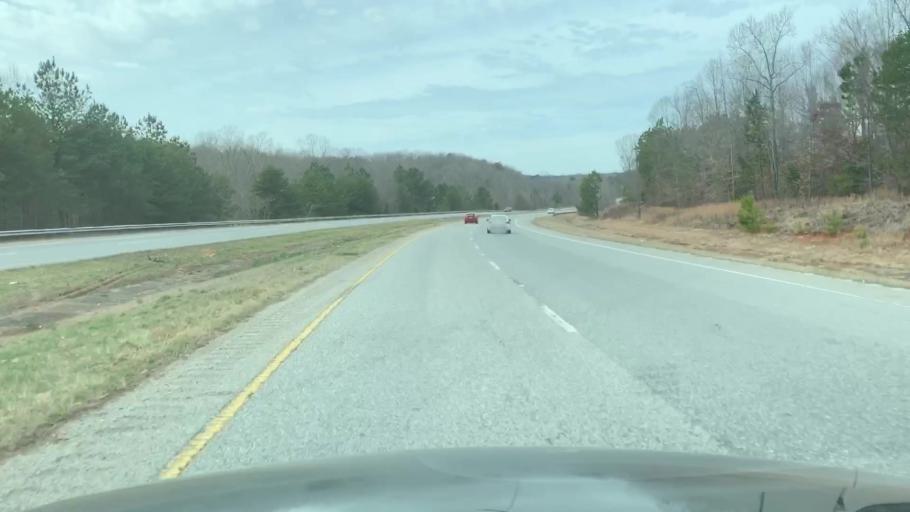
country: US
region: South Carolina
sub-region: Greenville County
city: Golden Grove
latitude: 34.7238
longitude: -82.3969
